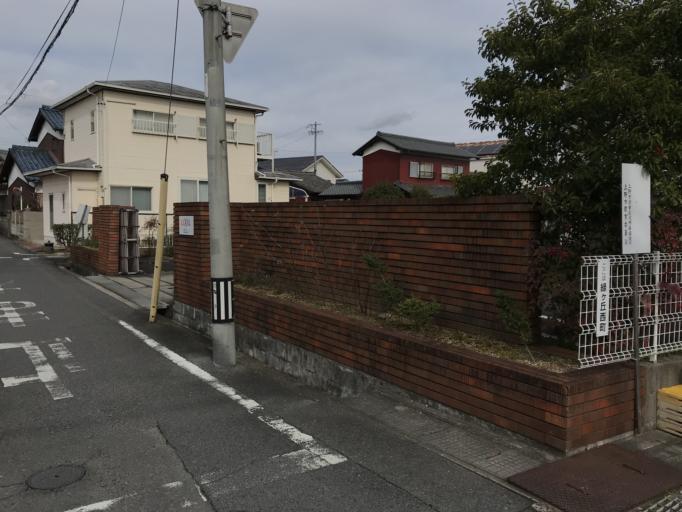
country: JP
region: Mie
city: Ueno-ebisumachi
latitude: 34.7592
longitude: 136.1372
